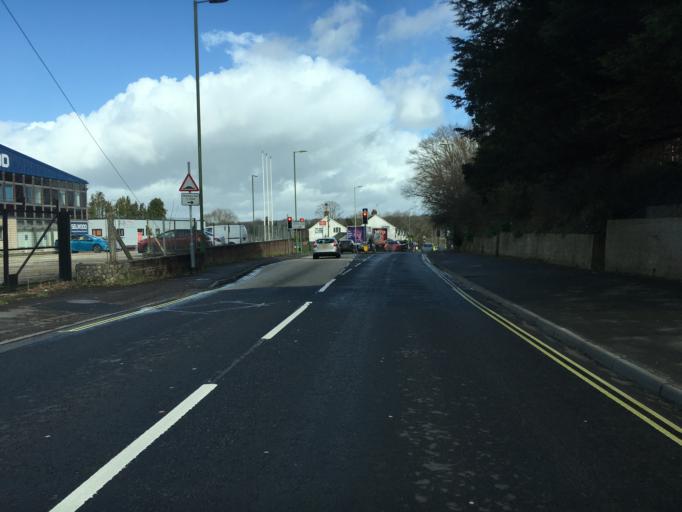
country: GB
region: England
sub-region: Hampshire
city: Chandlers Ford
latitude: 50.9806
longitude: -1.3846
